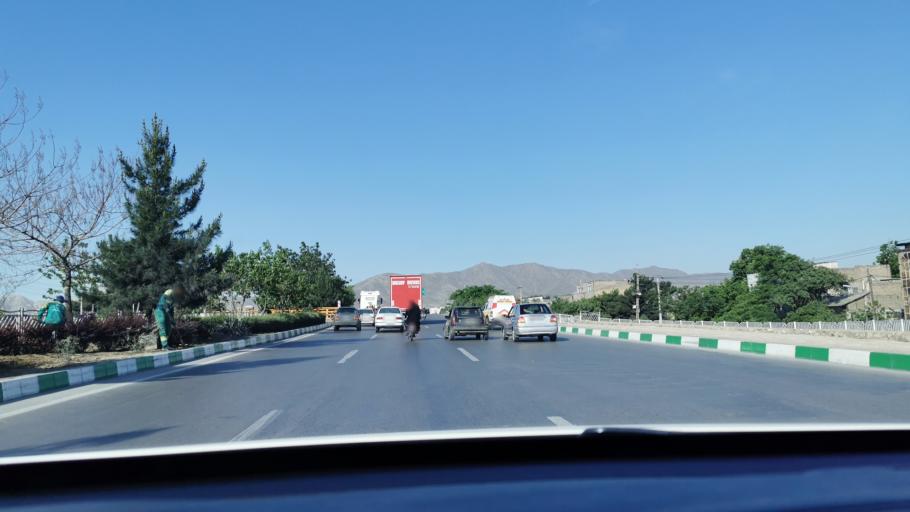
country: IR
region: Razavi Khorasan
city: Mashhad
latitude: 36.2547
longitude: 59.6176
